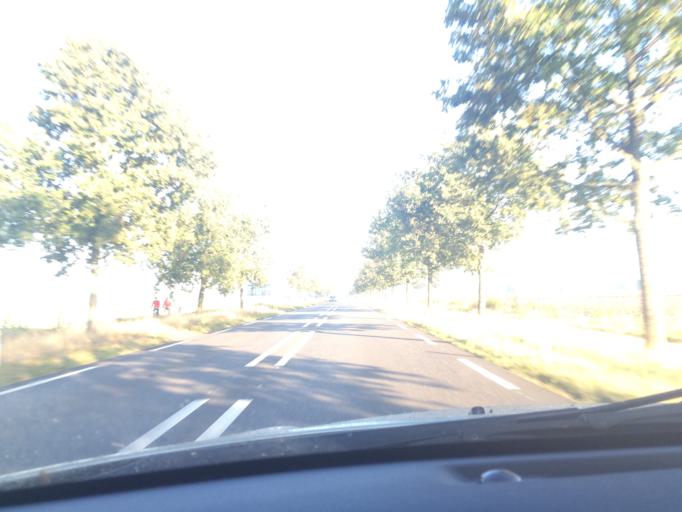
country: NL
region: North Brabant
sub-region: Gemeente Baarle-Nassau
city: Baarle-Nassau
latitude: 51.5116
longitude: 4.9614
